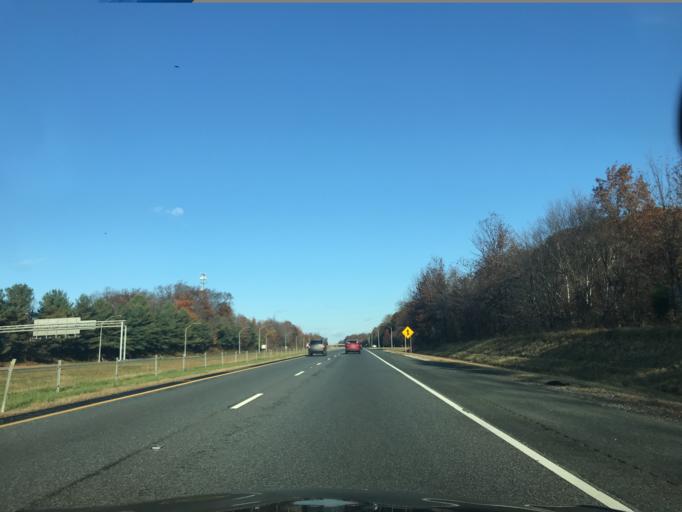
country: US
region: Maryland
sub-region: Baltimore County
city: Owings Mills
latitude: 39.4147
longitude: -76.7943
